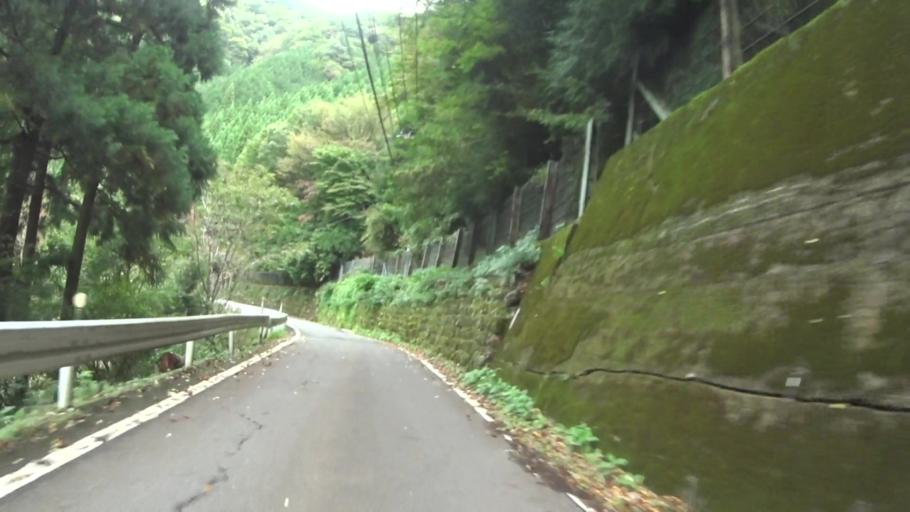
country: JP
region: Fukui
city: Obama
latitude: 35.3066
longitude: 135.6992
